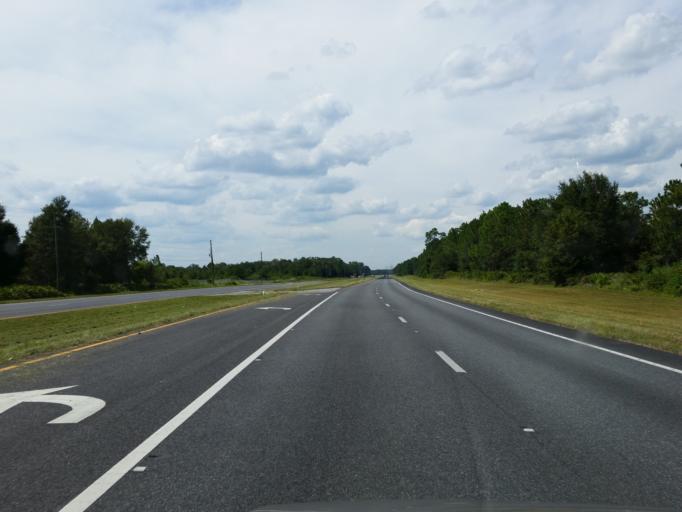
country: US
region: Florida
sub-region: Sumter County
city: Wildwood
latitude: 28.8532
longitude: -82.0678
